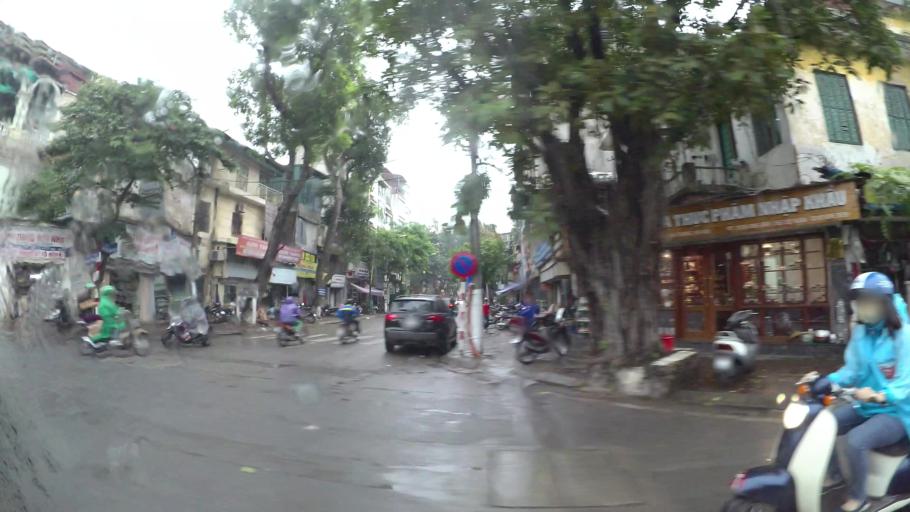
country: VN
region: Ha Noi
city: Hai BaTrung
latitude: 21.0141
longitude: 105.8557
